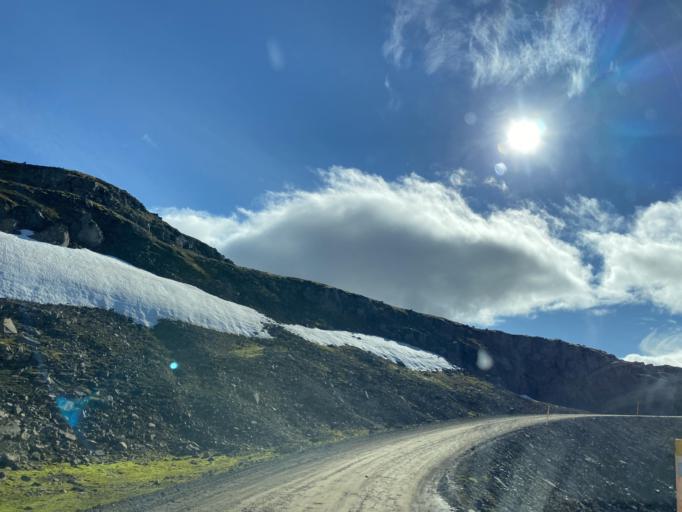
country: IS
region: East
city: Eskifjoerdur
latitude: 65.1675
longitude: -14.1303
